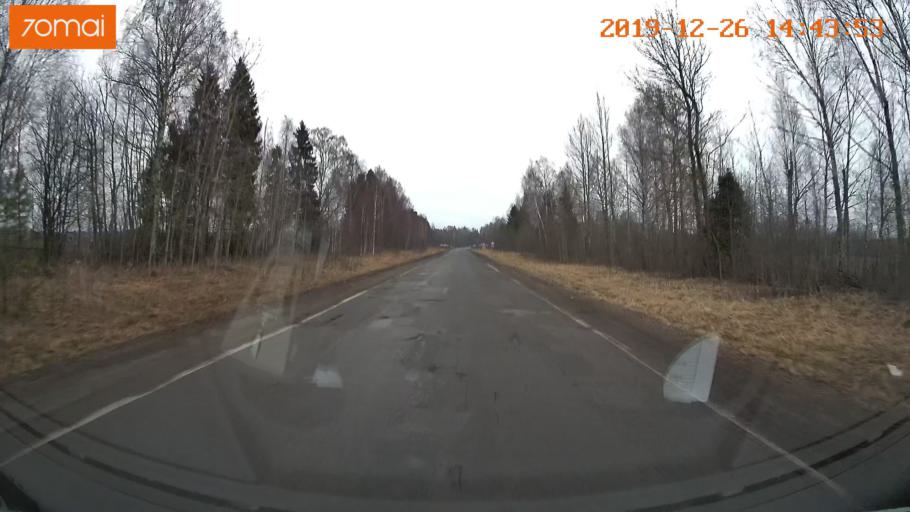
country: RU
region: Jaroslavl
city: Poshekhon'ye
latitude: 58.3528
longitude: 39.0452
